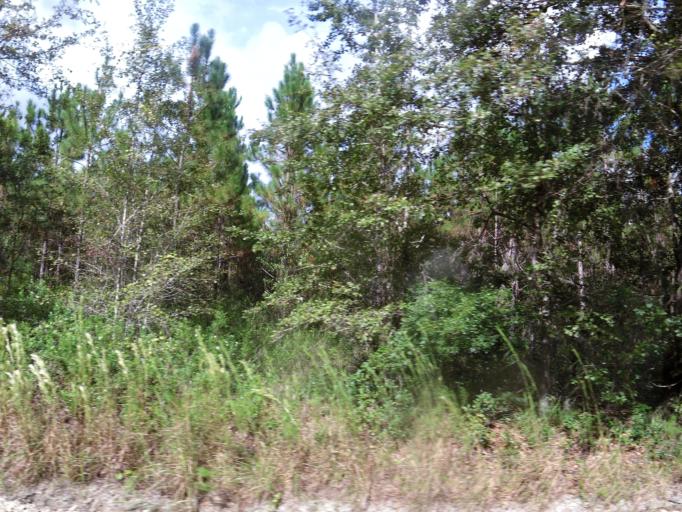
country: US
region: Florida
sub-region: Nassau County
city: Hilliard
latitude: 30.6060
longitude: -82.0718
